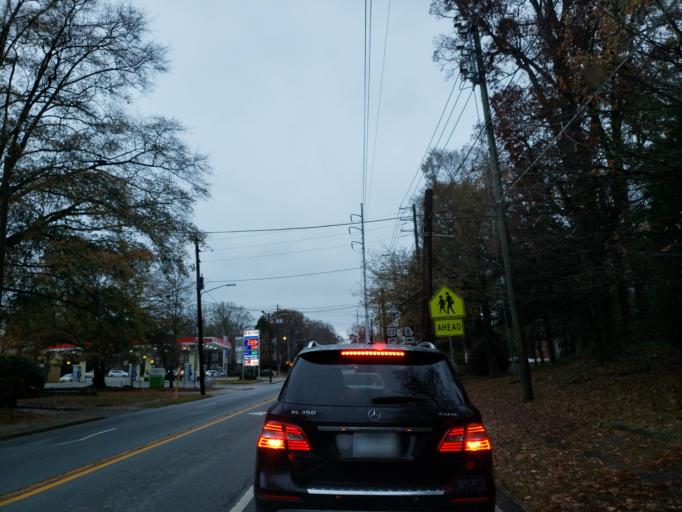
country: US
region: Georgia
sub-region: DeKalb County
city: Druid Hills
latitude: 33.7727
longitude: -84.3490
